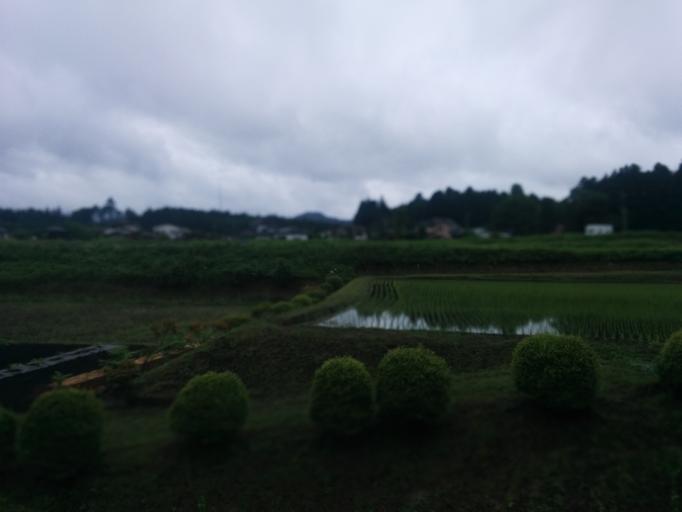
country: JP
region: Tochigi
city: Imaichi
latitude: 36.6727
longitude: 139.7252
